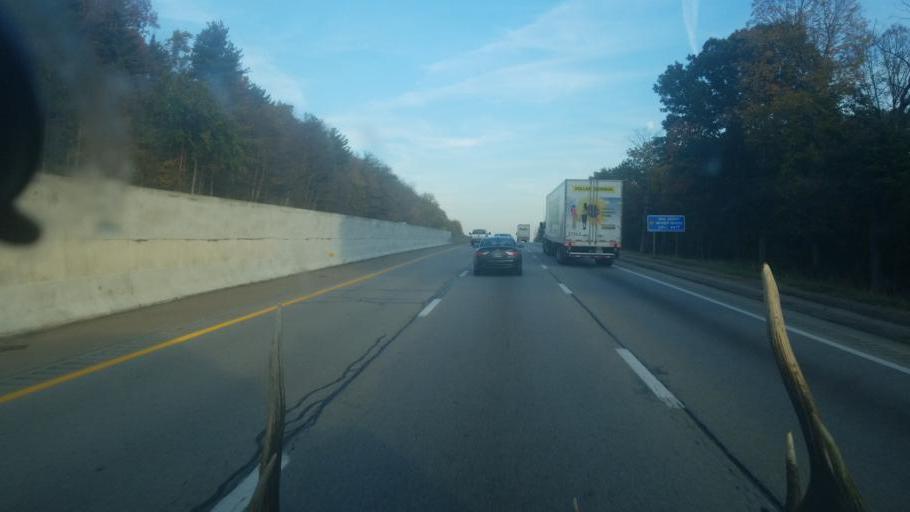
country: US
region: Ohio
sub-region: Perry County
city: Thornport
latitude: 39.9425
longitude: -82.3869
